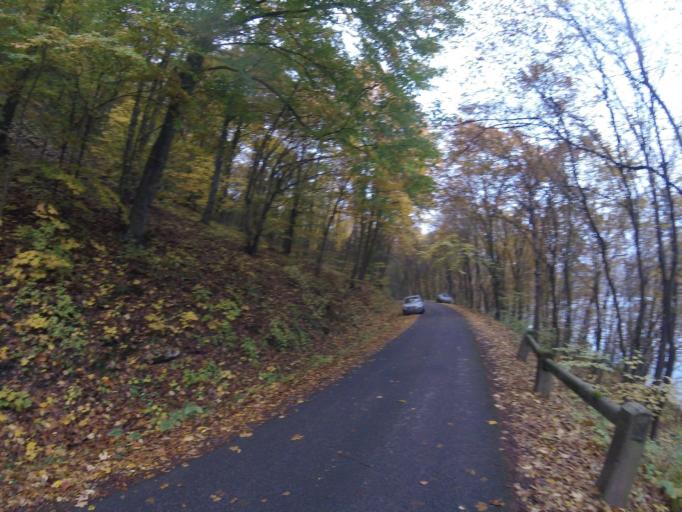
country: HU
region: Borsod-Abauj-Zemplen
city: Putnok
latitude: 48.2056
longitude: 20.4651
